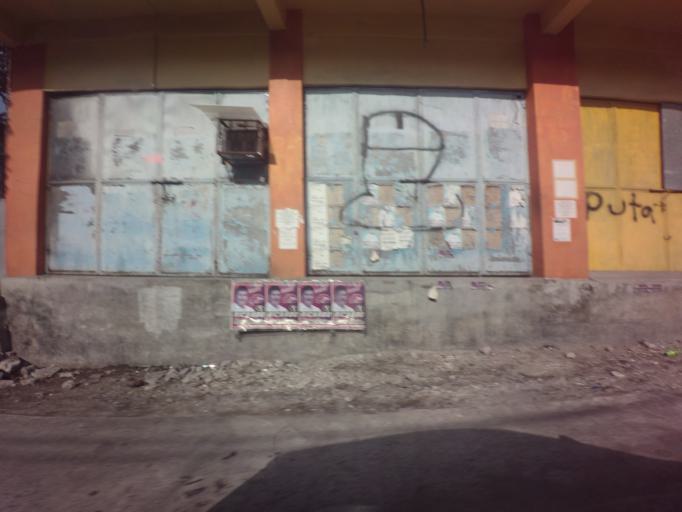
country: PH
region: Calabarzon
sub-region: Province of Rizal
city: Taguig
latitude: 14.4961
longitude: 121.0591
